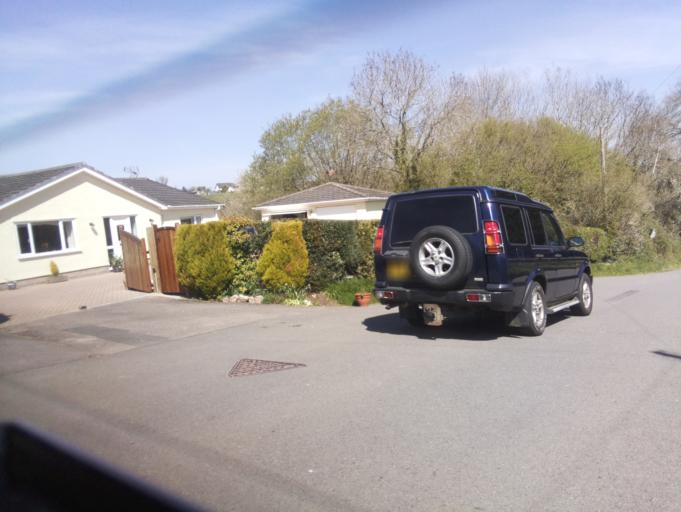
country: GB
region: Wales
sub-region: Monmouthshire
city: Caldicot
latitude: 51.6402
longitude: -2.7505
